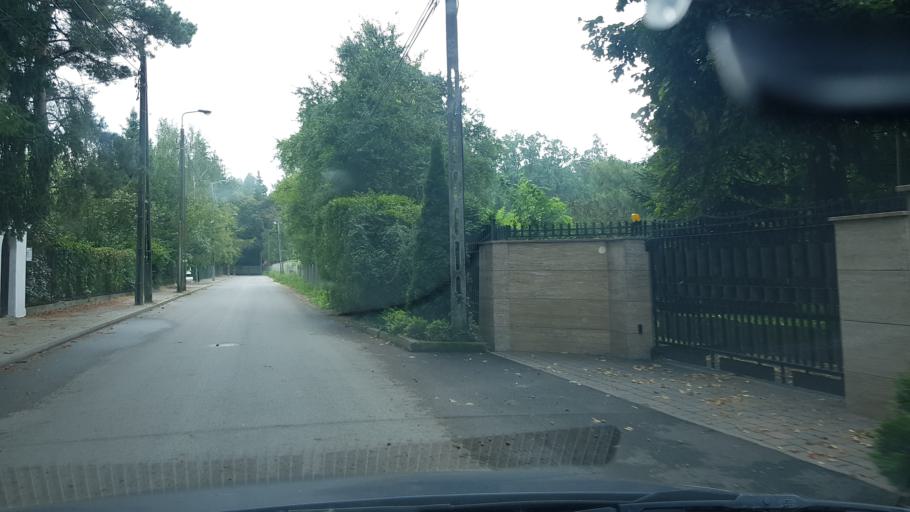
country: PL
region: Masovian Voivodeship
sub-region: Powiat piaseczynski
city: Konstancin-Jeziorna
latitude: 52.1022
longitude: 21.1072
